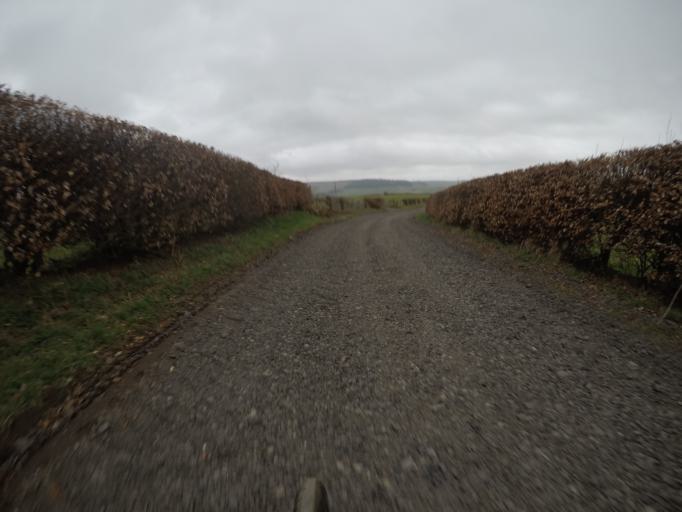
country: GB
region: Scotland
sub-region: East Ayrshire
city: Newmilns
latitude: 55.6228
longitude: -4.3428
